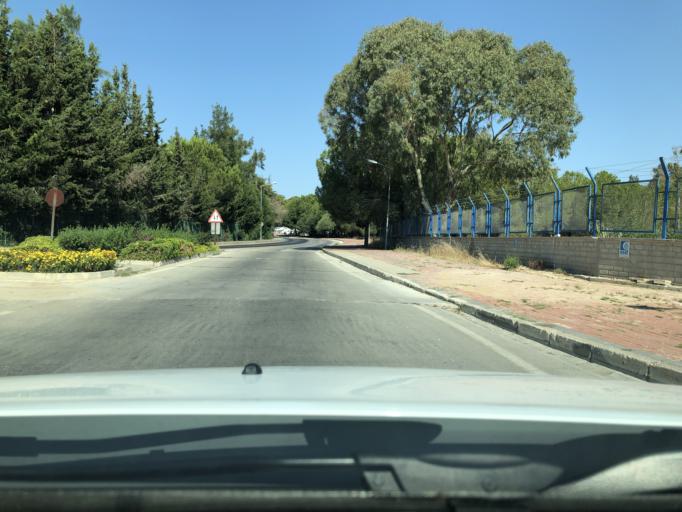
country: TR
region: Antalya
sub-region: Manavgat
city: Manavgat
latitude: 36.7583
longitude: 31.4365
